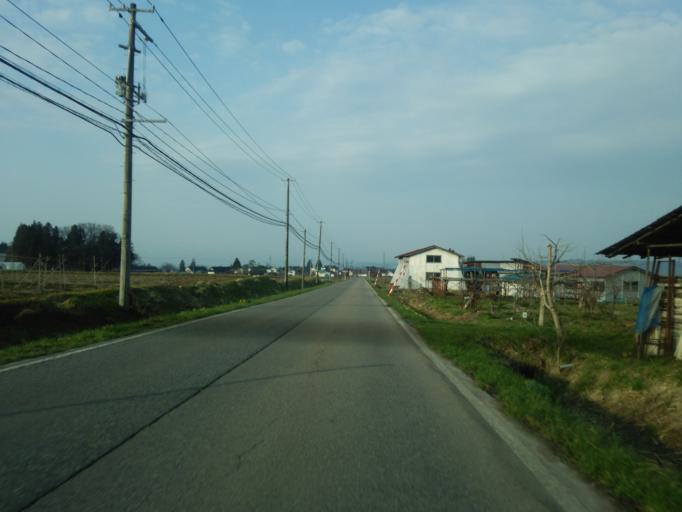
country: JP
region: Fukushima
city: Kitakata
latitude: 37.6816
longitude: 139.9001
